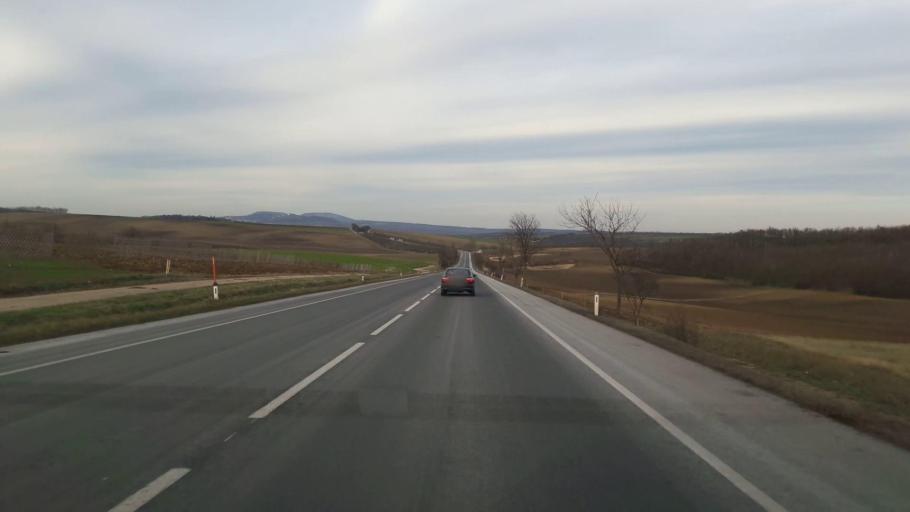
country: AT
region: Lower Austria
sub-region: Politischer Bezirk Mistelbach
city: Drasenhofen
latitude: 48.7189
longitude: 16.6556
